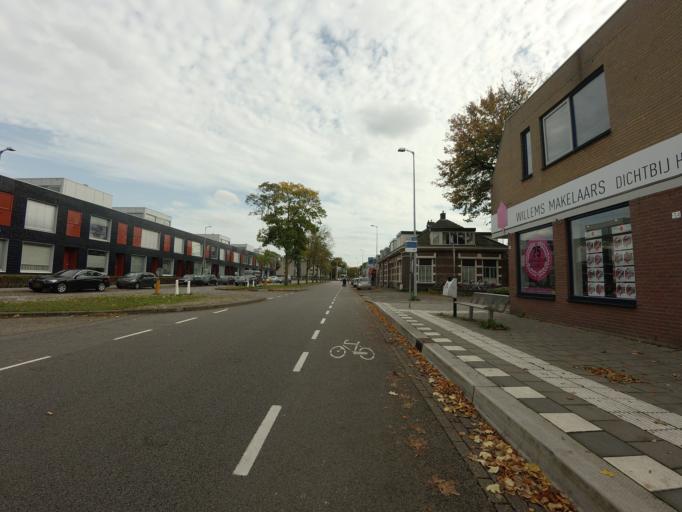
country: NL
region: North Brabant
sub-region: Gemeente Breda
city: Breda
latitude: 51.5829
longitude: 4.7795
